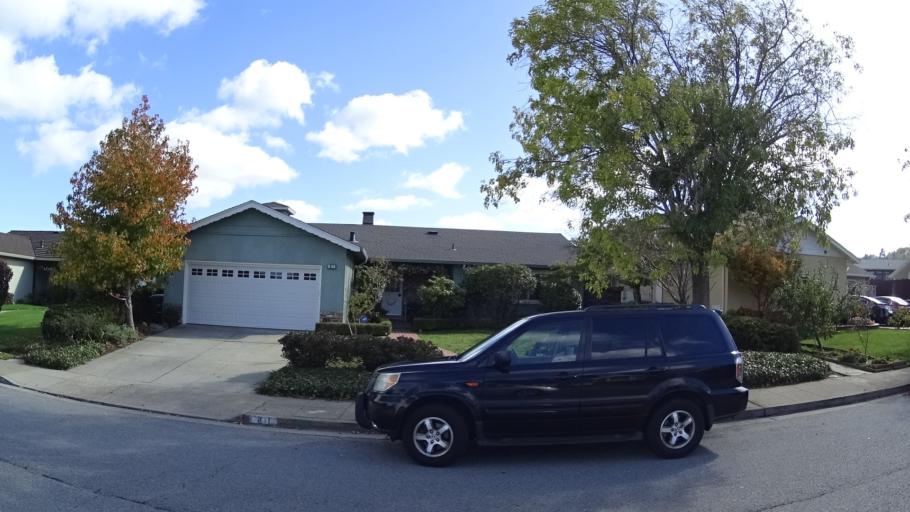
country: US
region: California
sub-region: San Mateo County
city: Millbrae
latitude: 37.5920
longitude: -122.3909
